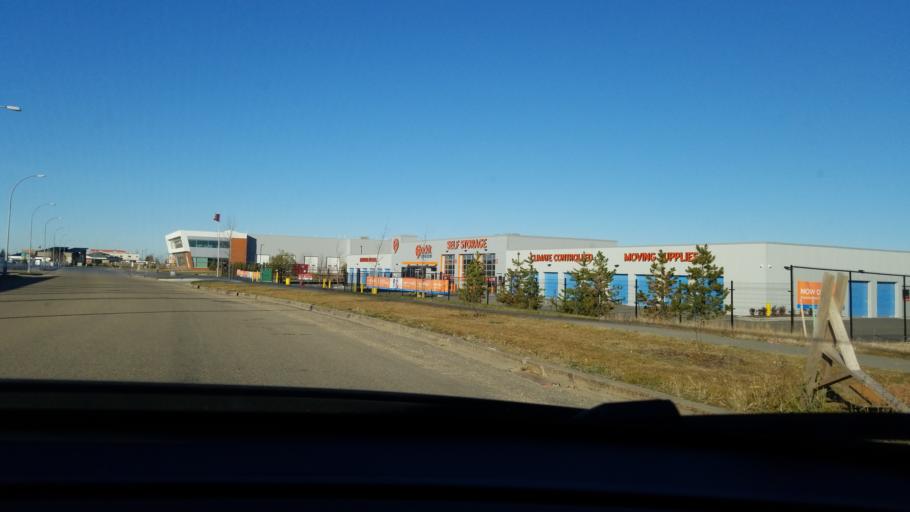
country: CA
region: Alberta
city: Sherwood Park
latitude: 53.5453
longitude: -113.3057
